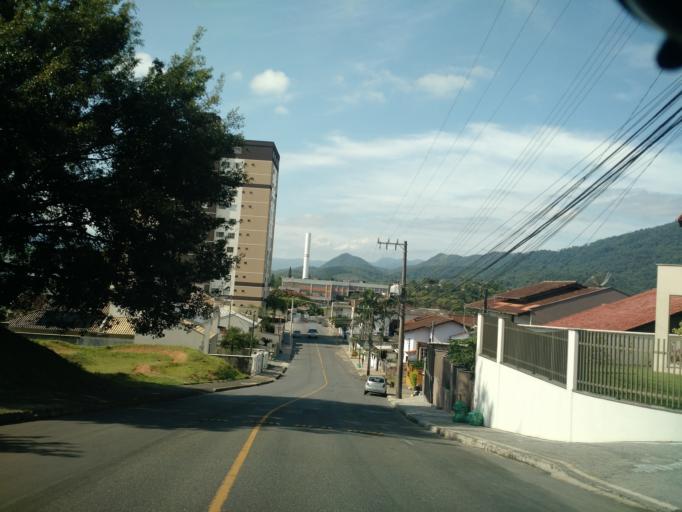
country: BR
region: Santa Catarina
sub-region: Jaragua Do Sul
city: Jaragua do Sul
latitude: -26.4848
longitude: -49.1023
